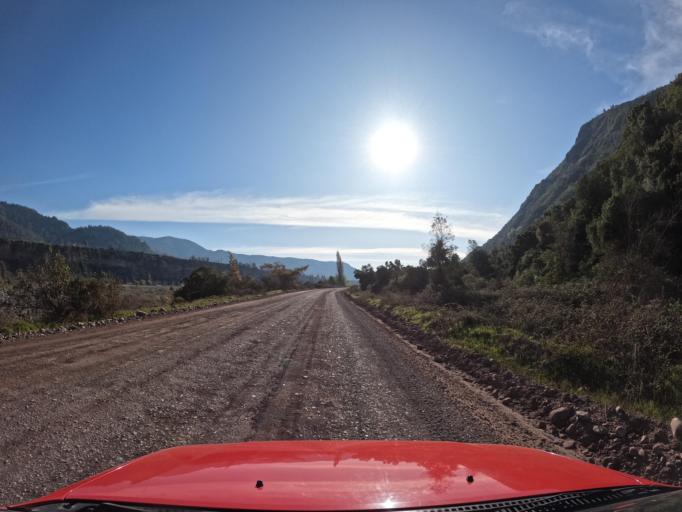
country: CL
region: Maule
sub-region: Provincia de Curico
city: Teno
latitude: -35.0011
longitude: -70.8394
